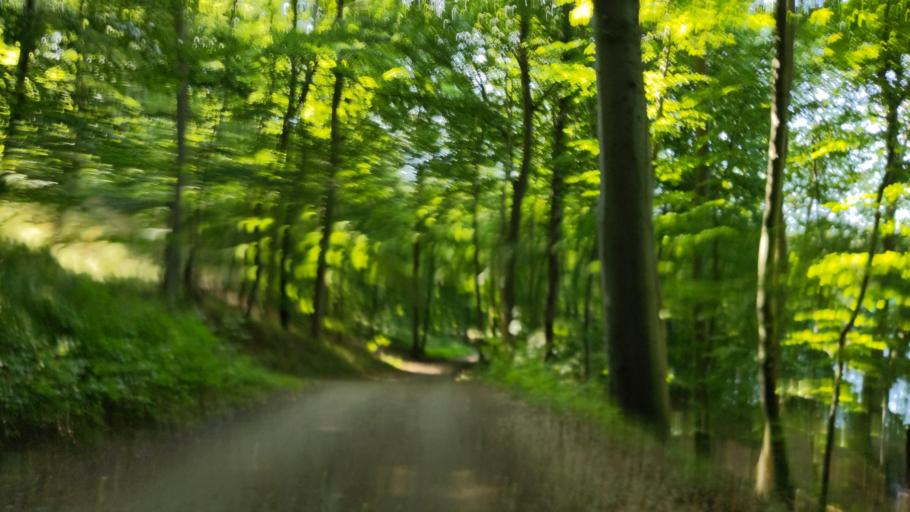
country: DE
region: Schleswig-Holstein
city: Malente
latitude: 54.1601
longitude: 10.5355
